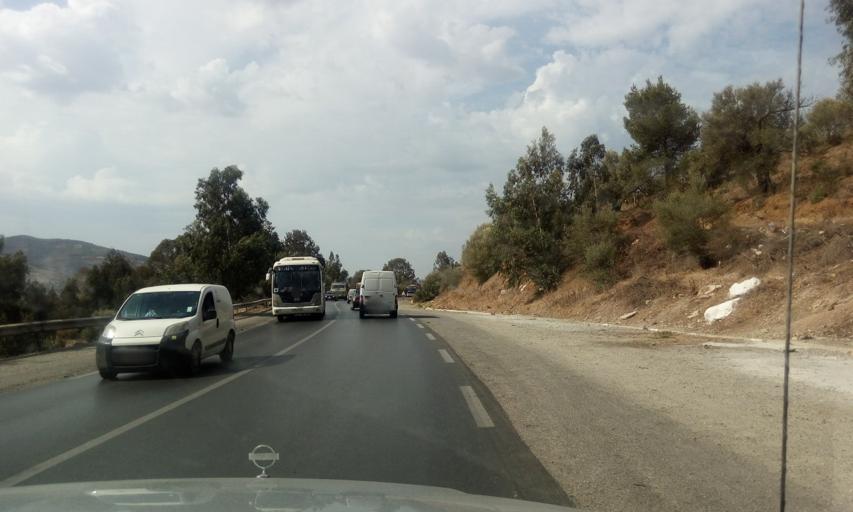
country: DZ
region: Bejaia
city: Seddouk
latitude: 36.5964
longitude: 4.6757
